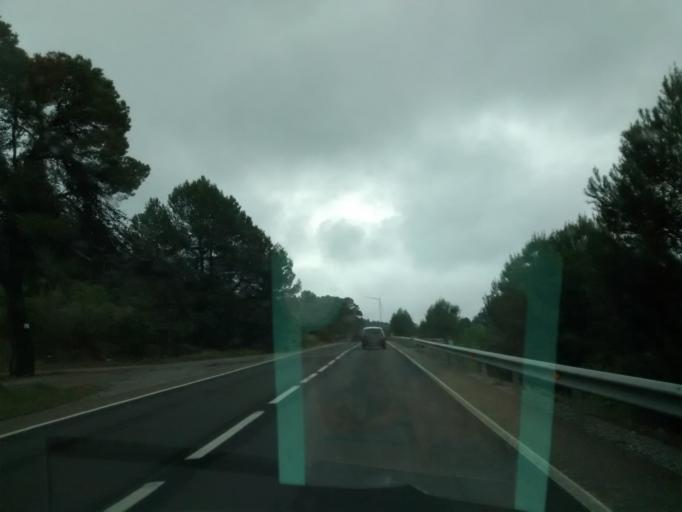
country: ES
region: Catalonia
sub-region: Provincia de Tarragona
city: Batea
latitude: 41.0631
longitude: 0.3398
